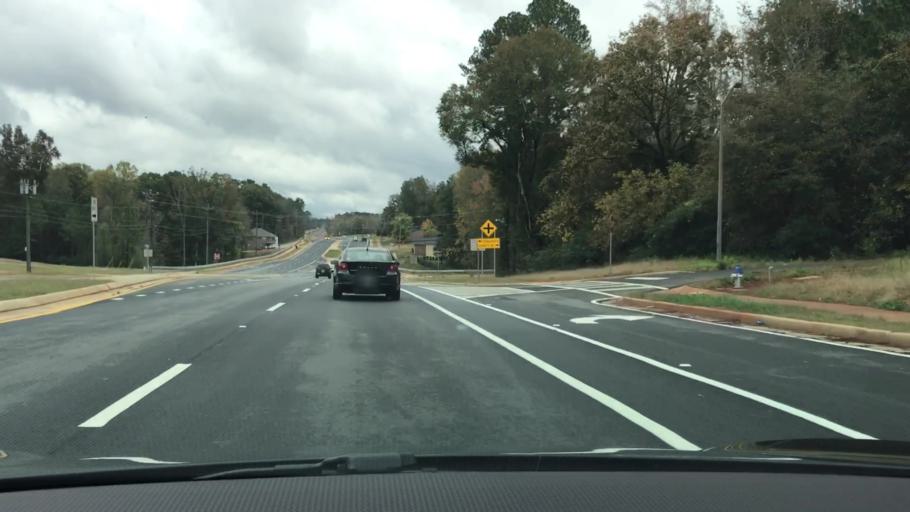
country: US
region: Georgia
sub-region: Oconee County
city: Watkinsville
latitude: 33.8983
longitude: -83.4623
